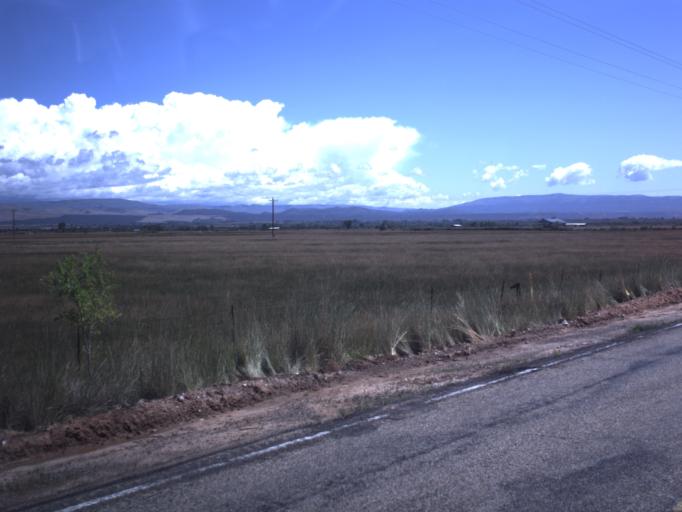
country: US
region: Utah
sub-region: Duchesne County
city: Roosevelt
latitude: 40.4329
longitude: -109.9699
